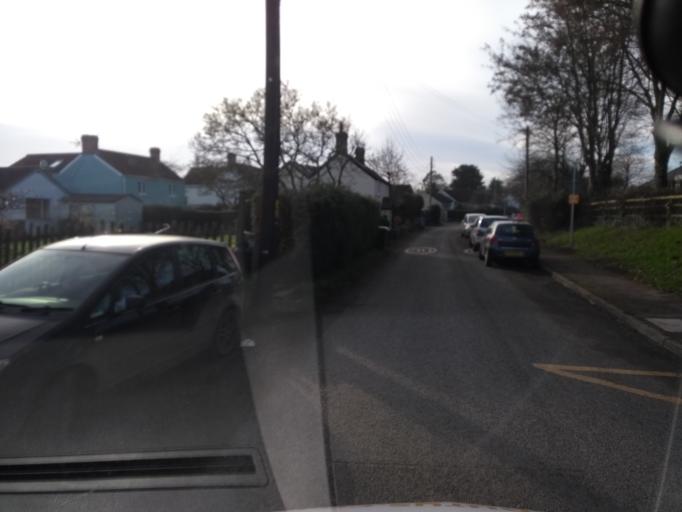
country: GB
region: England
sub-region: Somerset
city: Creech Saint Michael
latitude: 51.0198
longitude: -2.9732
